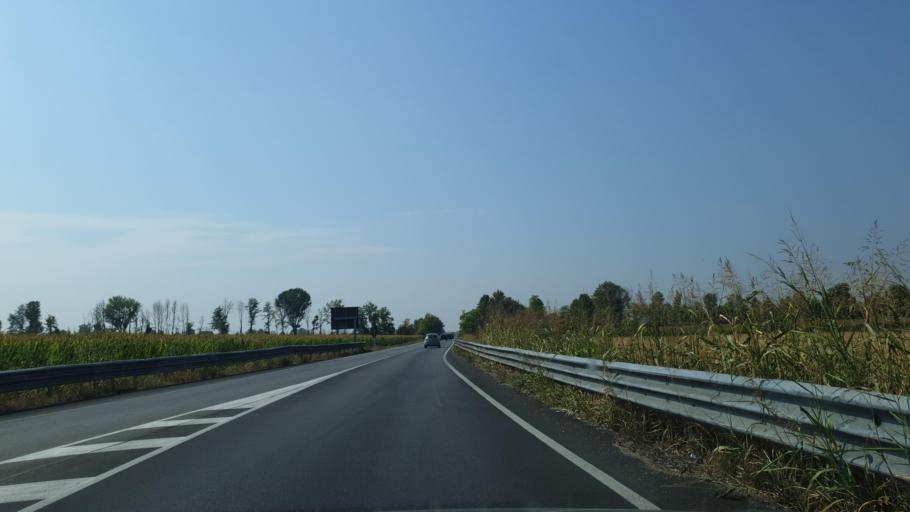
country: IT
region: Lombardy
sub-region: Provincia di Brescia
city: Ghedi
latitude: 45.3863
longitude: 10.2489
